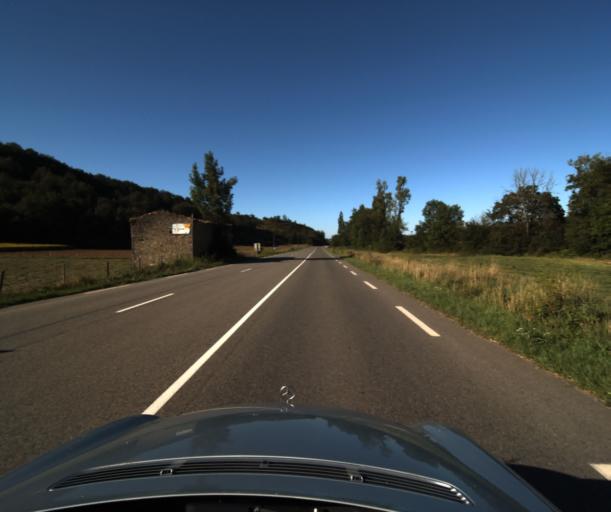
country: FR
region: Midi-Pyrenees
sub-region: Departement de l'Ariege
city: Mirepoix
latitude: 43.0092
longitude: 1.8859
